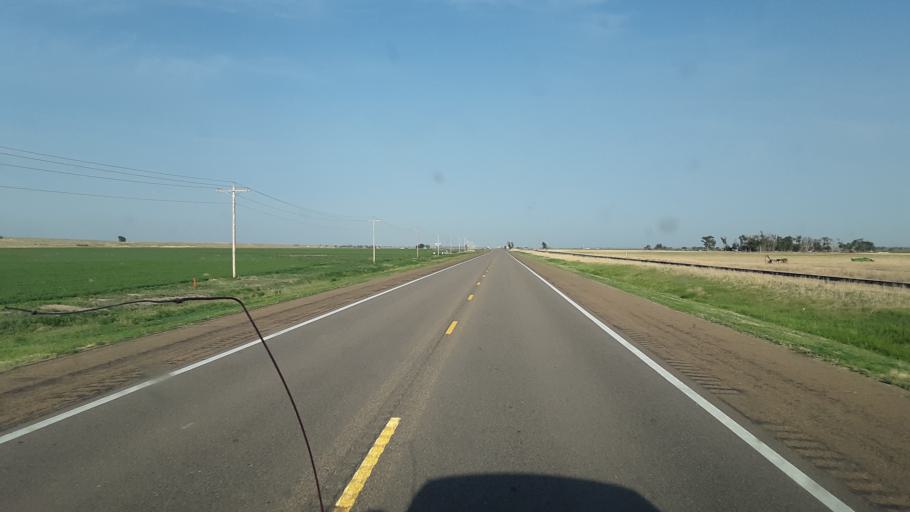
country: US
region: Kansas
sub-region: Hamilton County
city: Syracuse
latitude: 38.0196
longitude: -101.9024
